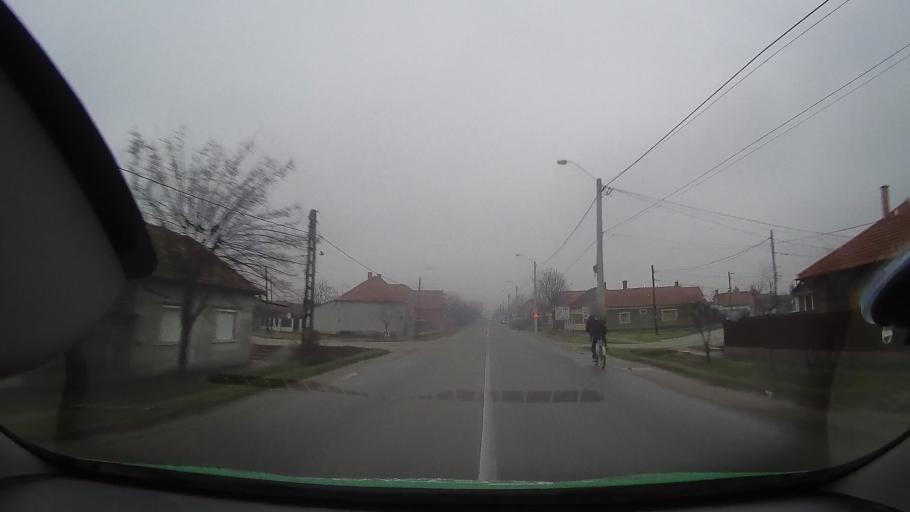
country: RO
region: Bihor
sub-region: Municipiul Salonta
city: Salonta
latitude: 46.7964
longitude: 21.6696
